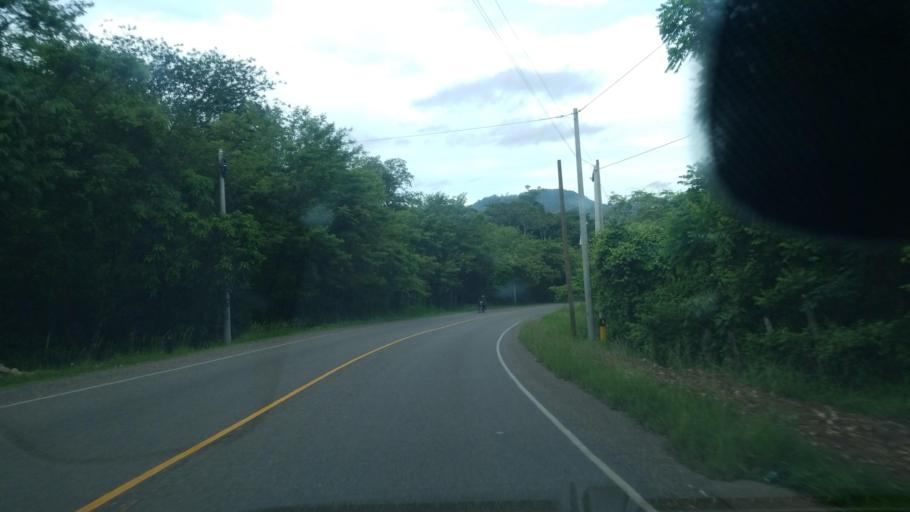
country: HN
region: Santa Barbara
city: Ceguaca
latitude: 14.8126
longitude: -88.1967
